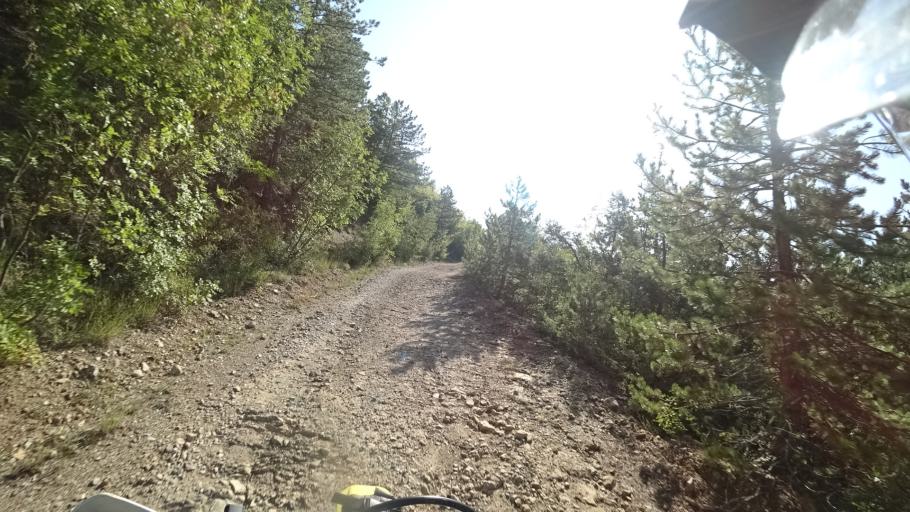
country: HR
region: Sibensko-Kniniska
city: Knin
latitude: 44.1351
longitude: 16.1783
